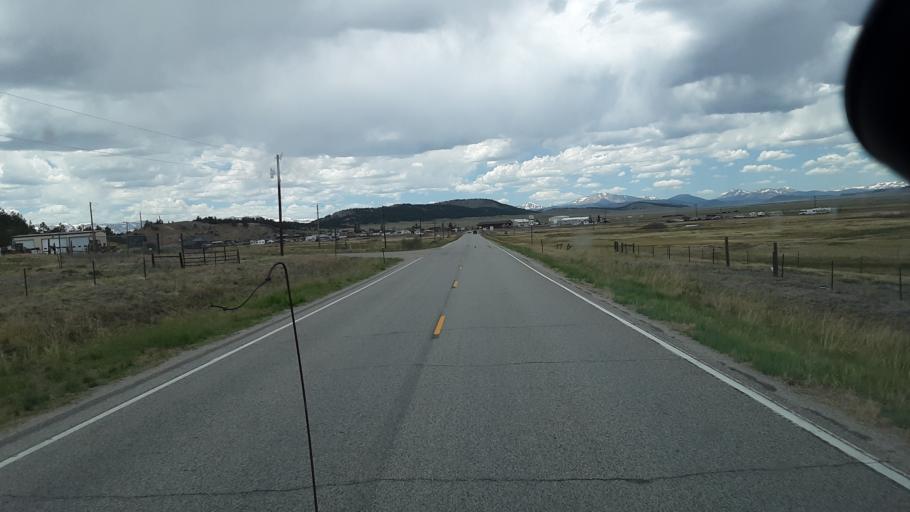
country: US
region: Colorado
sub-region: Park County
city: Fairplay
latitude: 39.0169
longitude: -105.7892
